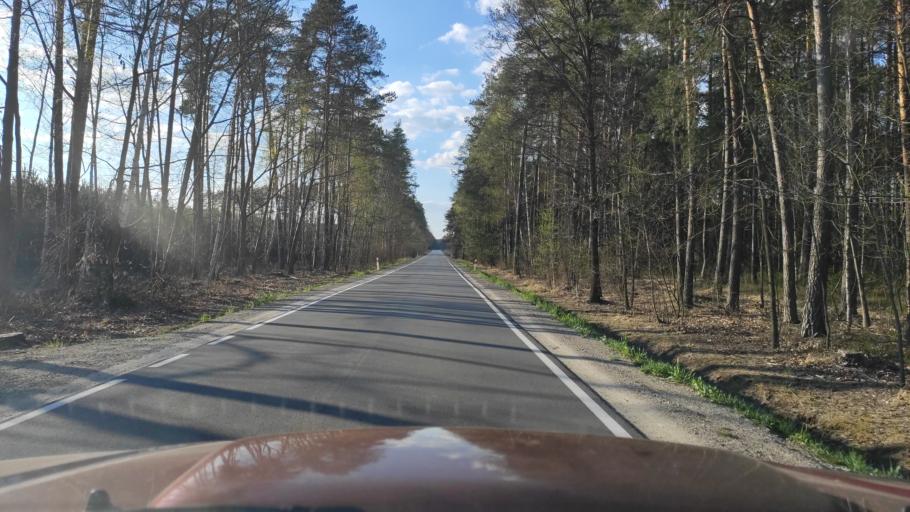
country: PL
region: Masovian Voivodeship
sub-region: Powiat zwolenski
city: Zwolen
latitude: 51.3926
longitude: 21.5469
